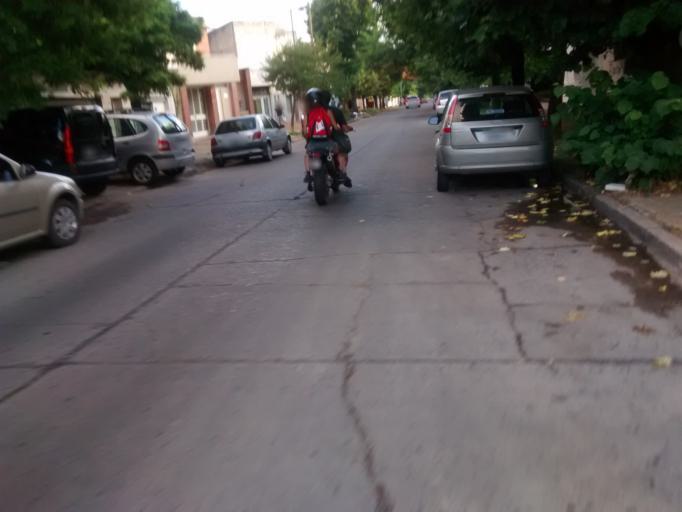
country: AR
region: Buenos Aires
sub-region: Partido de La Plata
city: La Plata
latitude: -34.9161
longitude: -57.9672
